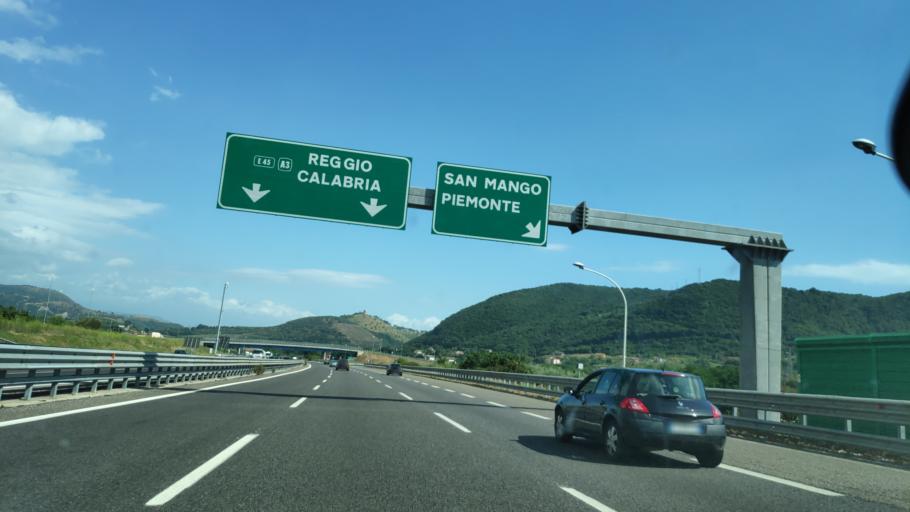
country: IT
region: Campania
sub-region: Provincia di Salerno
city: San Mango Piemonte
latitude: 40.6916
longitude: 14.8361
